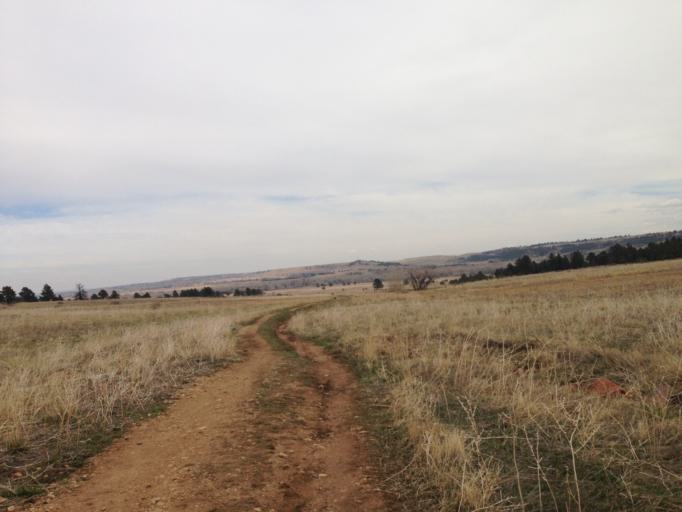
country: US
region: Colorado
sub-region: Boulder County
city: Boulder
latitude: 39.9547
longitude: -105.2636
